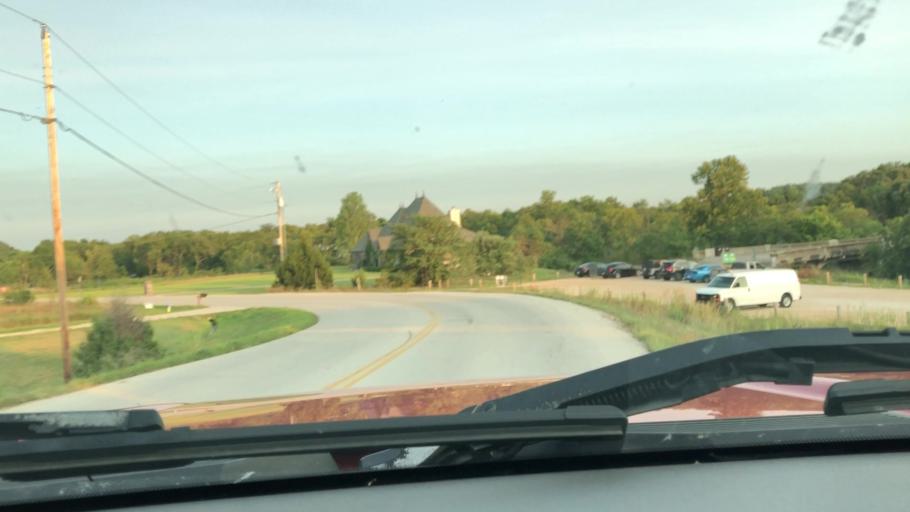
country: US
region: Missouri
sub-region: Jasper County
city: Joplin
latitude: 37.0215
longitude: -94.5127
